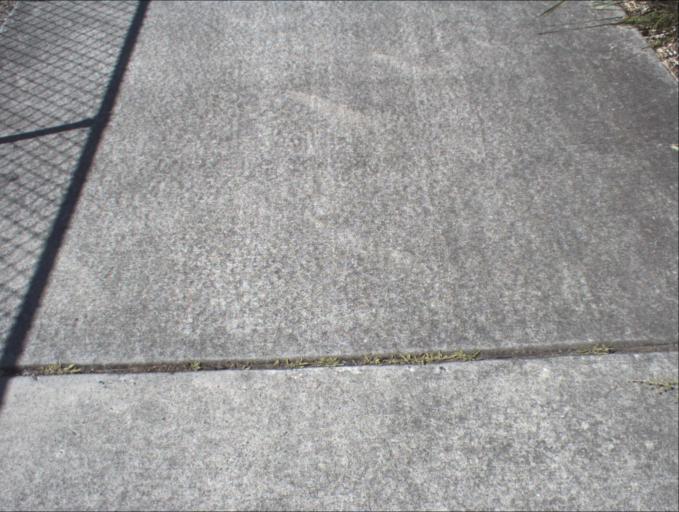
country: AU
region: Queensland
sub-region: Logan
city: Waterford West
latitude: -27.7055
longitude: 153.1602
